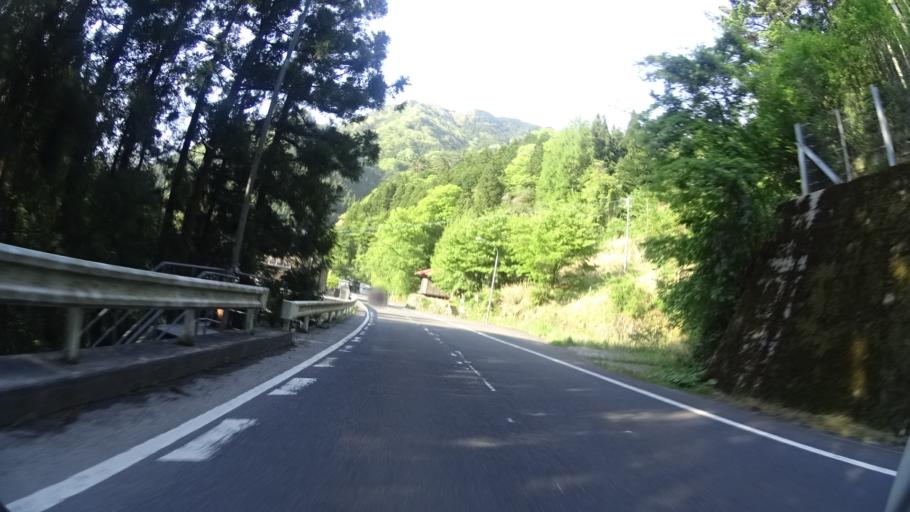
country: JP
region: Tokushima
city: Ikedacho
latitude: 33.8681
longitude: 133.8724
